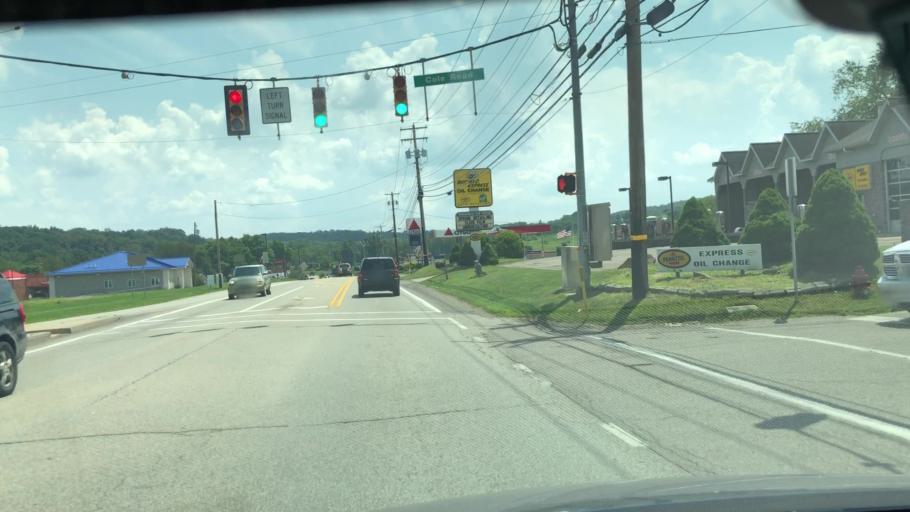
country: US
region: Pennsylvania
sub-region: Armstrong County
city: Freeport
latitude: 40.7015
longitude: -79.7214
